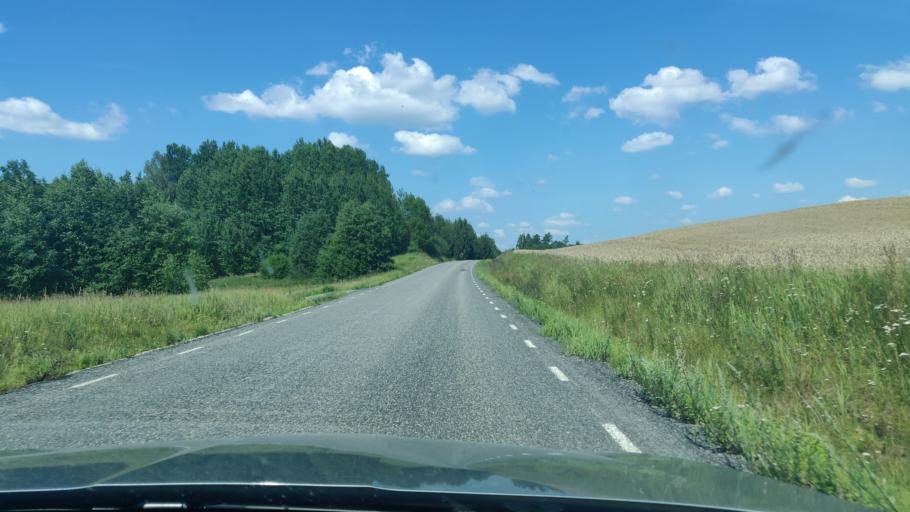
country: EE
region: Tartu
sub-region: Elva linn
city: Elva
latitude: 58.1473
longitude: 26.4743
